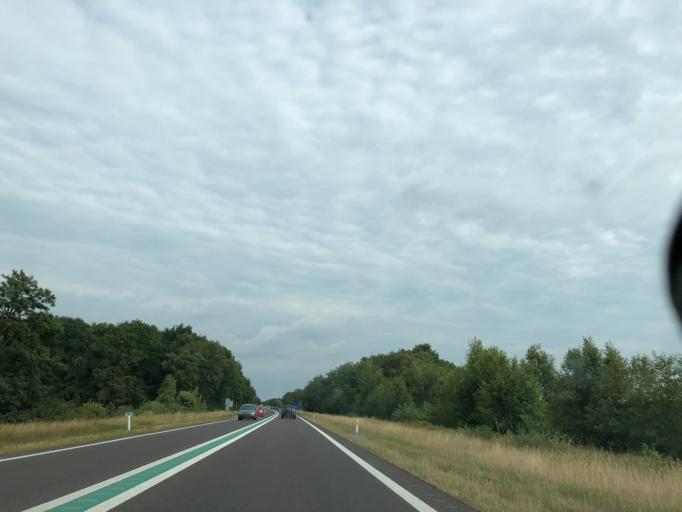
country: NL
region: Drenthe
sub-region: Gemeente Tynaarlo
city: Tynaarlo
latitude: 53.0905
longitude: 6.6442
